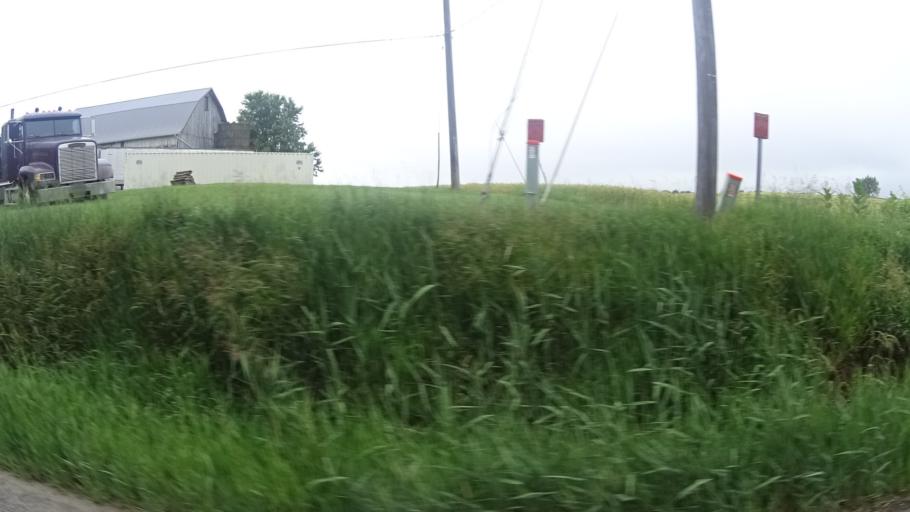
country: US
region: Ohio
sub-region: Erie County
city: Milan
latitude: 41.3418
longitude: -82.5816
